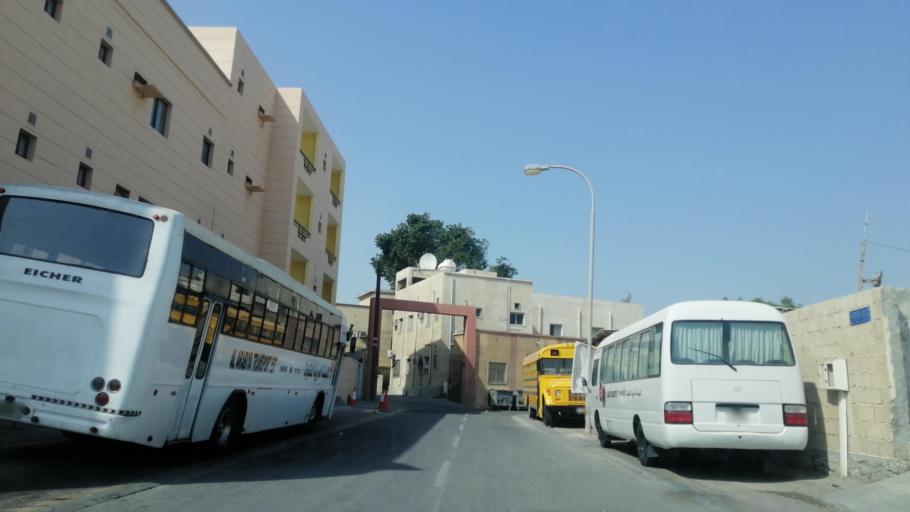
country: BH
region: Muharraq
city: Al Hadd
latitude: 26.2536
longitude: 50.6353
